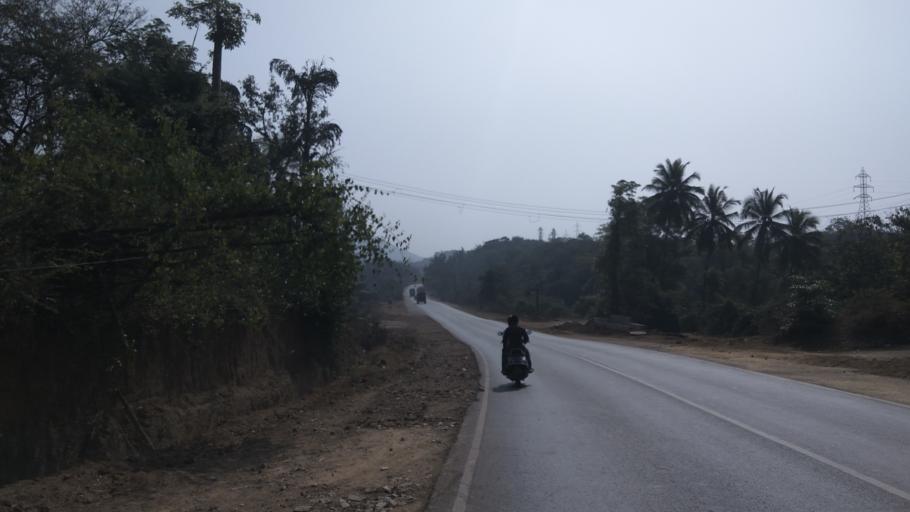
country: IN
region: Goa
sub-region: North Goa
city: Palle
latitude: 15.3905
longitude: 74.1234
